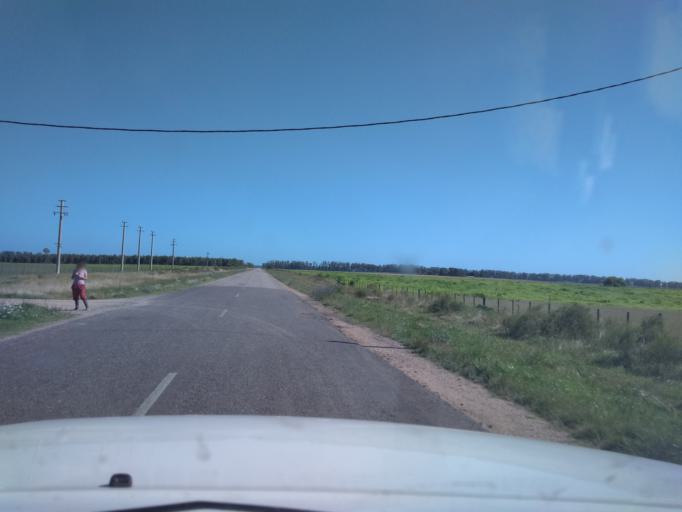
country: UY
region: Canelones
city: San Ramon
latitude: -34.1540
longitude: -55.9463
